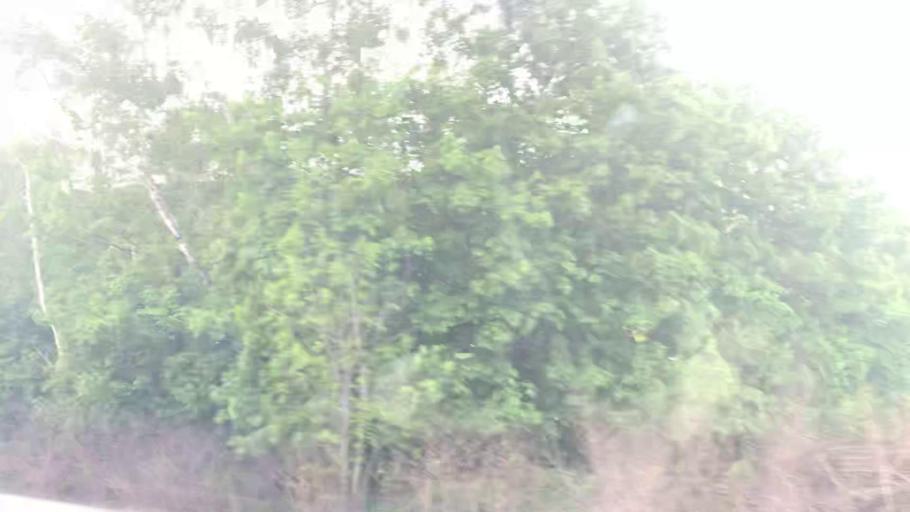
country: PL
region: Lower Silesian Voivodeship
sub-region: Powiat walbrzyski
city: Walbrzych
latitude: 50.7689
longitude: 16.2540
